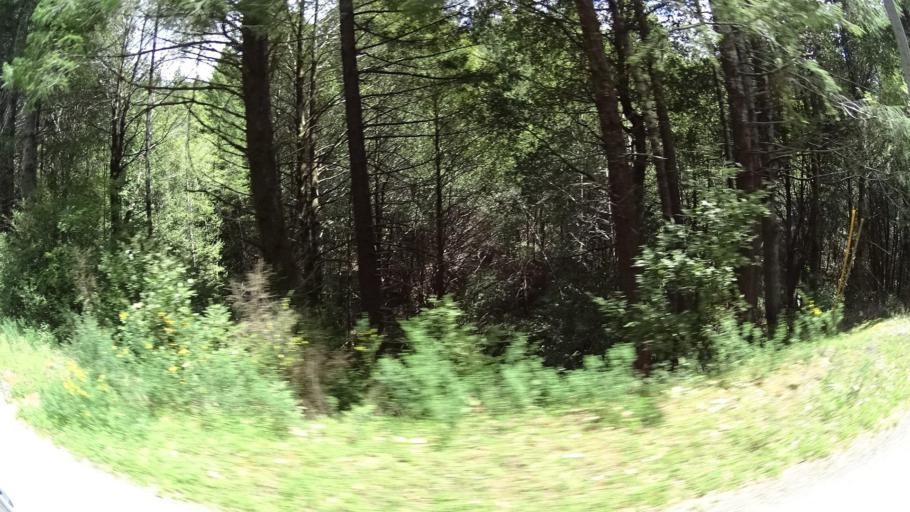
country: US
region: California
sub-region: Humboldt County
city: Redway
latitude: 40.0702
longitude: -123.9583
